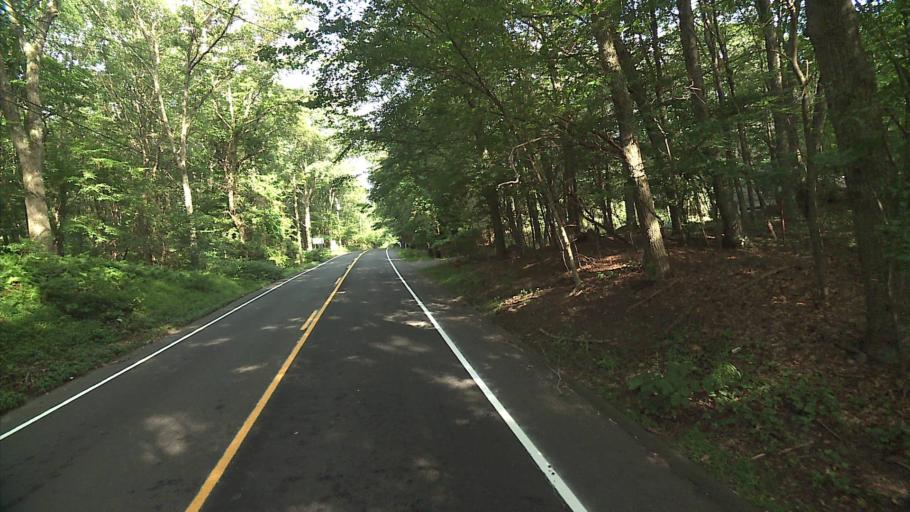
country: US
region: Connecticut
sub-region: New Haven County
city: Ansonia
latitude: 41.3594
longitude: -73.0450
